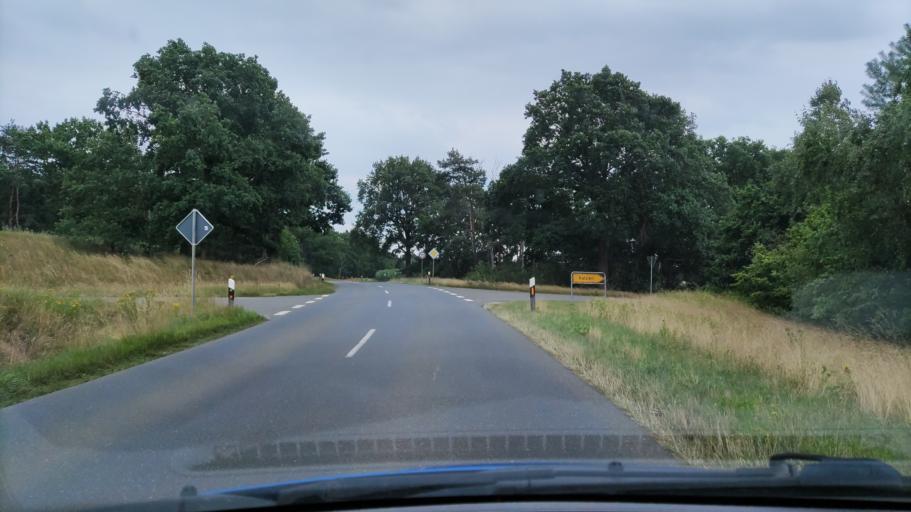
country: DE
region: Lower Saxony
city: Rosche
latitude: 53.0044
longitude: 10.7659
